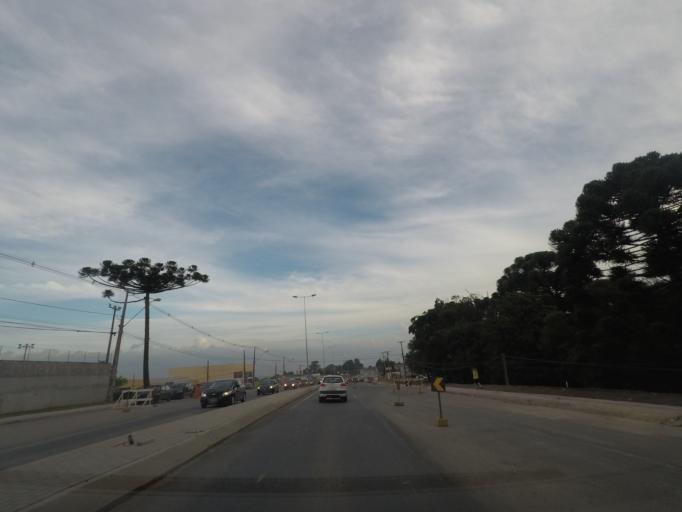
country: BR
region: Parana
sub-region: Colombo
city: Colombo
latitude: -25.3309
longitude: -49.2209
